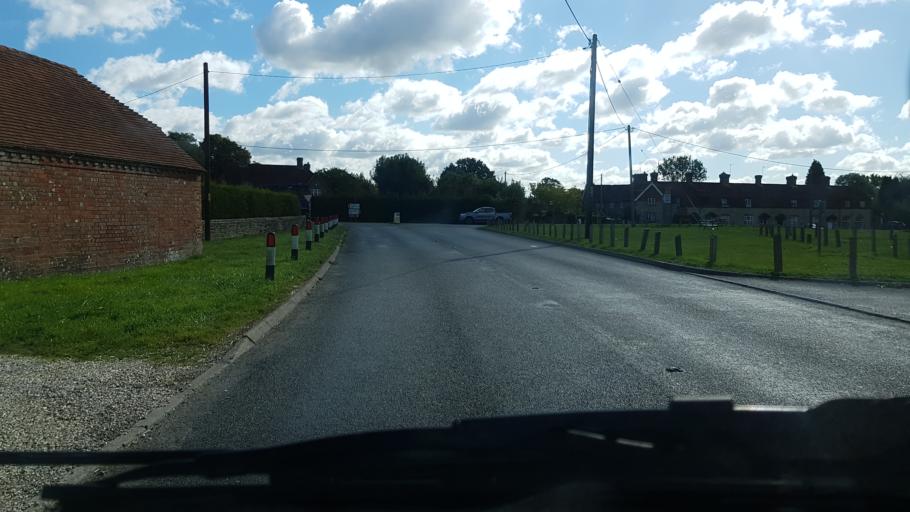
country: GB
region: England
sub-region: West Sussex
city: Billingshurst
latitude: 50.9993
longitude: -0.4715
